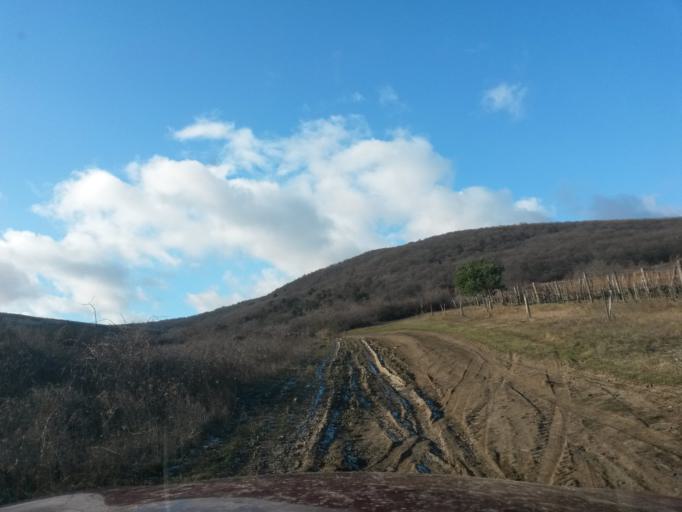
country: HU
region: Borsod-Abauj-Zemplen
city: Sarospatak
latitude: 48.3331
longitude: 21.5171
